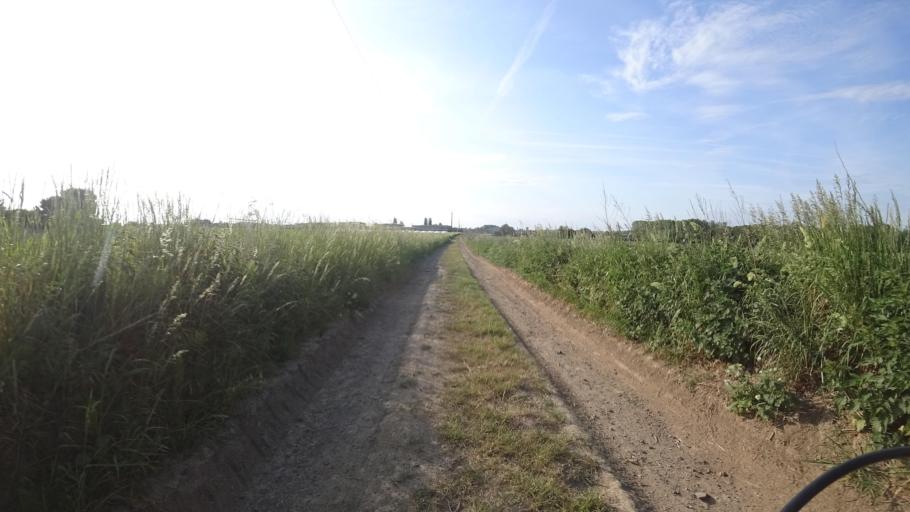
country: BE
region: Wallonia
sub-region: Province de Namur
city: Gembloux
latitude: 50.5825
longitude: 4.6965
